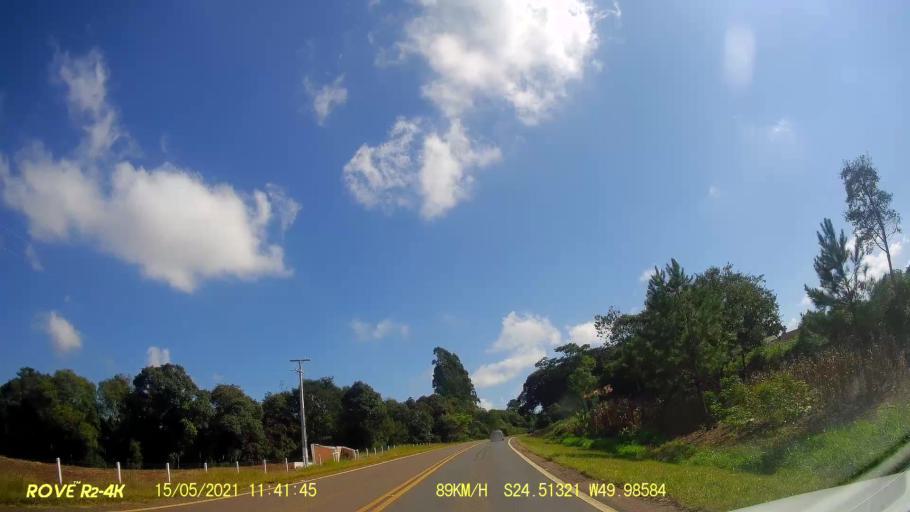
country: BR
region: Parana
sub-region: Pirai Do Sul
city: Pirai do Sul
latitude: -24.5133
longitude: -49.9858
